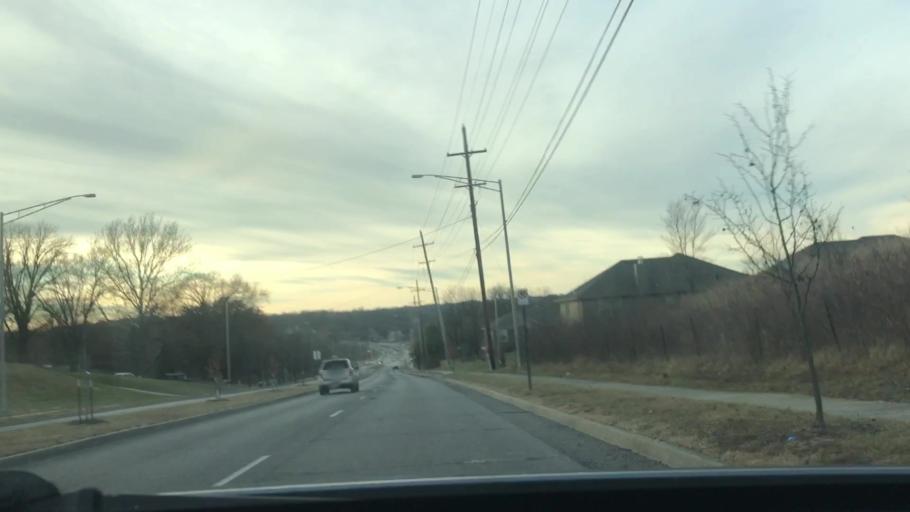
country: US
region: Missouri
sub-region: Platte County
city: Riverside
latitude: 39.2176
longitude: -94.6097
